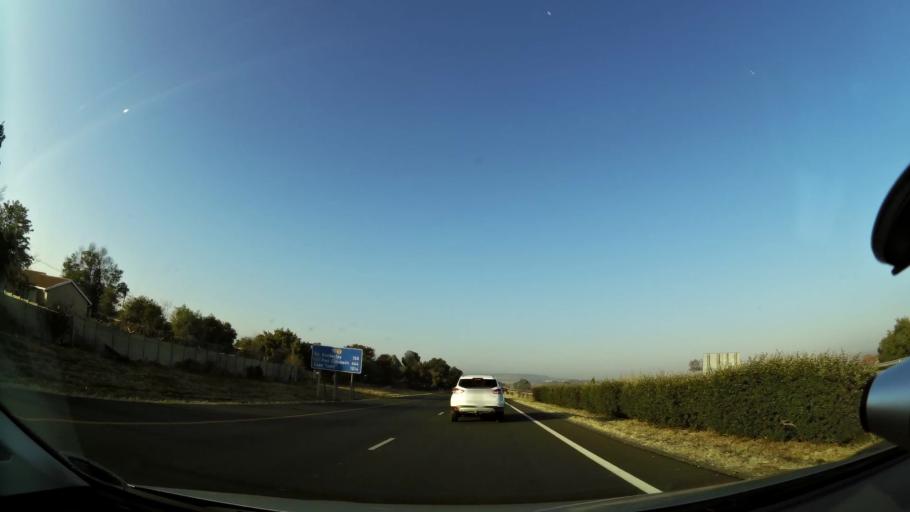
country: ZA
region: Orange Free State
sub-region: Mangaung Metropolitan Municipality
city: Bloemfontein
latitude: -29.1024
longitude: 26.1649
